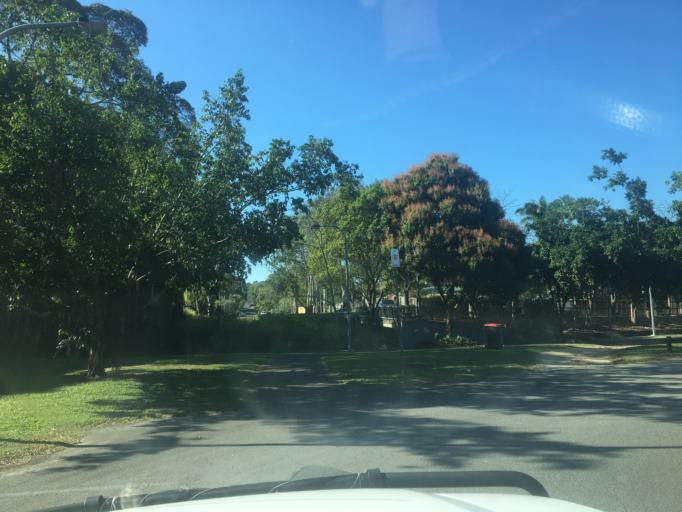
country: AU
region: Queensland
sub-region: Cairns
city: Woree
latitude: -16.9415
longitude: 145.7362
